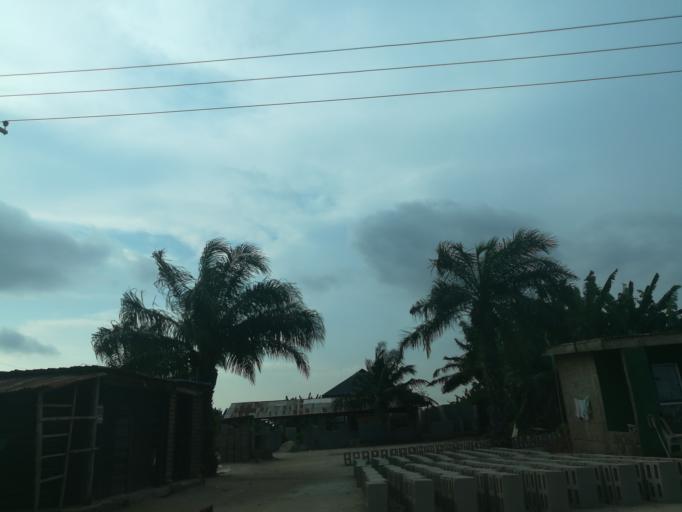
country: NG
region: Lagos
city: Ikorodu
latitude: 6.6112
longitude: 3.5963
